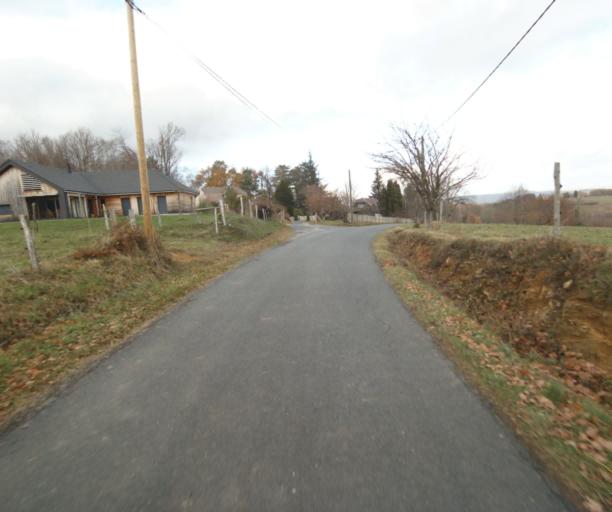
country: FR
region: Limousin
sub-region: Departement de la Correze
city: Sainte-Fortunade
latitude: 45.2192
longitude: 1.7908
